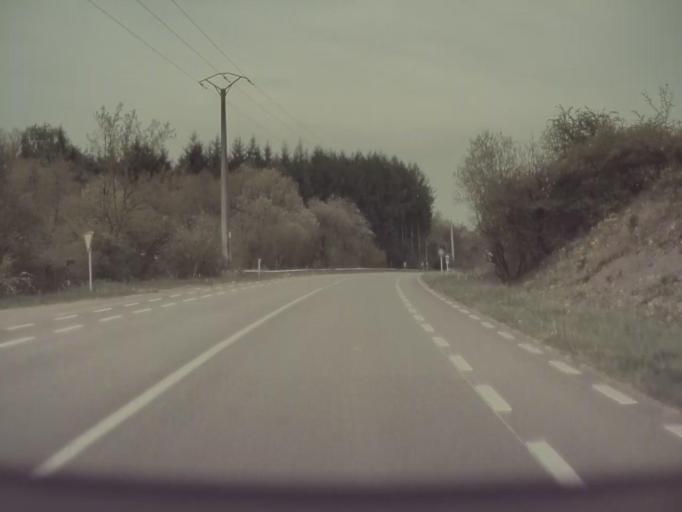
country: BE
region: Wallonia
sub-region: Province de Liege
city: Hamoir
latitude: 50.4081
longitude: 5.5079
